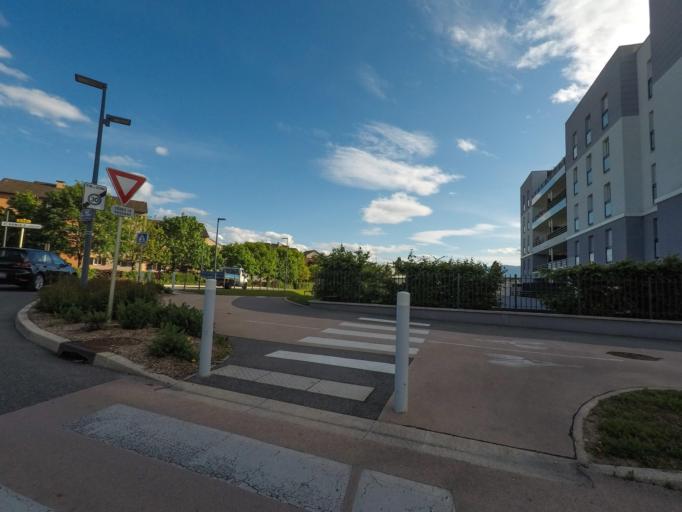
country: FR
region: Rhone-Alpes
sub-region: Departement de l'Ain
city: Saint-Genis-Pouilly
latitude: 46.2501
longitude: 6.0298
